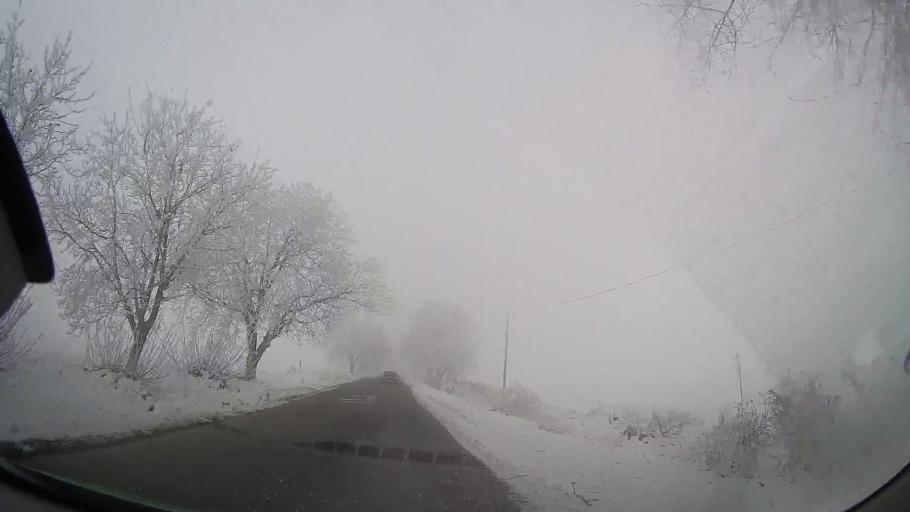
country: RO
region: Neamt
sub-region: Comuna Sabaoani
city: Sabaoani
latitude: 46.9882
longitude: 26.8631
